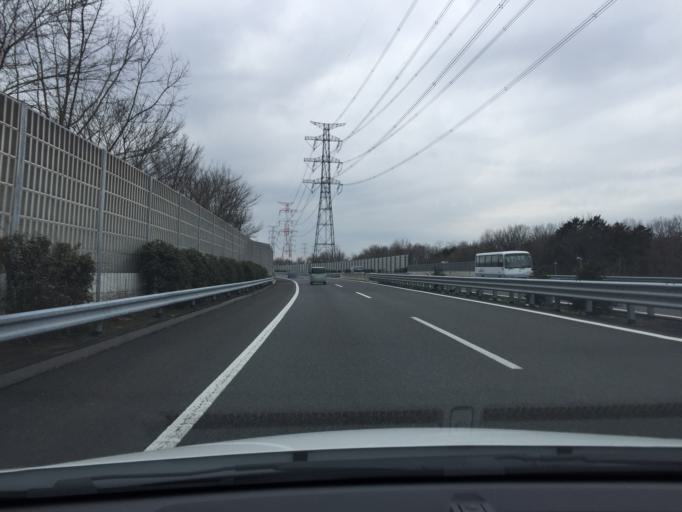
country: JP
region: Saitama
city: Sakado
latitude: 35.9583
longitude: 139.4316
